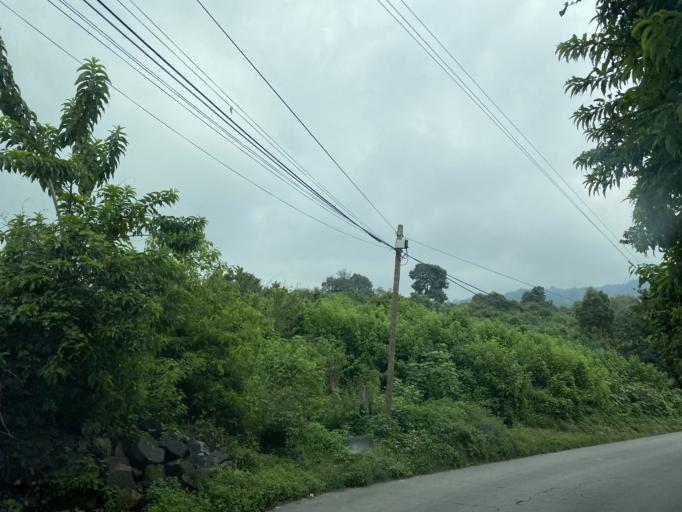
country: MX
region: Morelos
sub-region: Yecapixtla
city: Texcala
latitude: 18.9326
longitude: -98.8010
